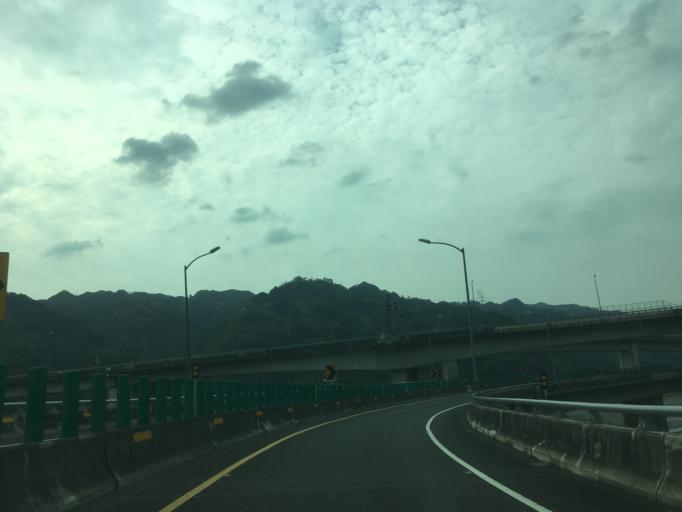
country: TW
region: Taiwan
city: Zhongxing New Village
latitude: 24.0032
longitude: 120.8129
